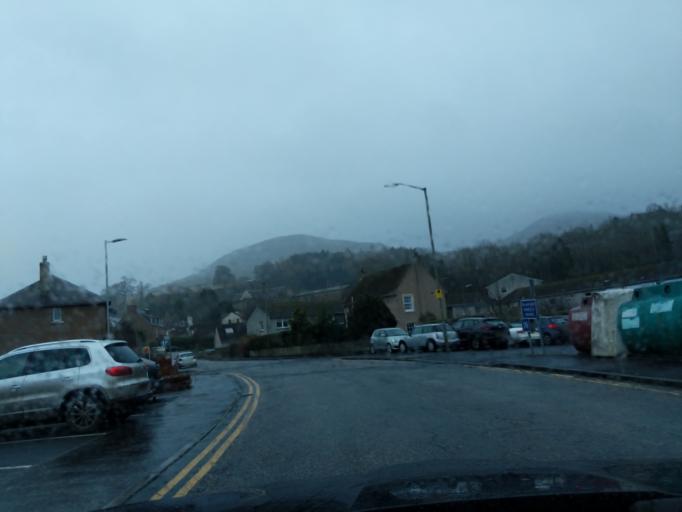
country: GB
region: Scotland
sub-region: The Scottish Borders
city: Melrose
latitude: 55.5983
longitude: -2.7232
